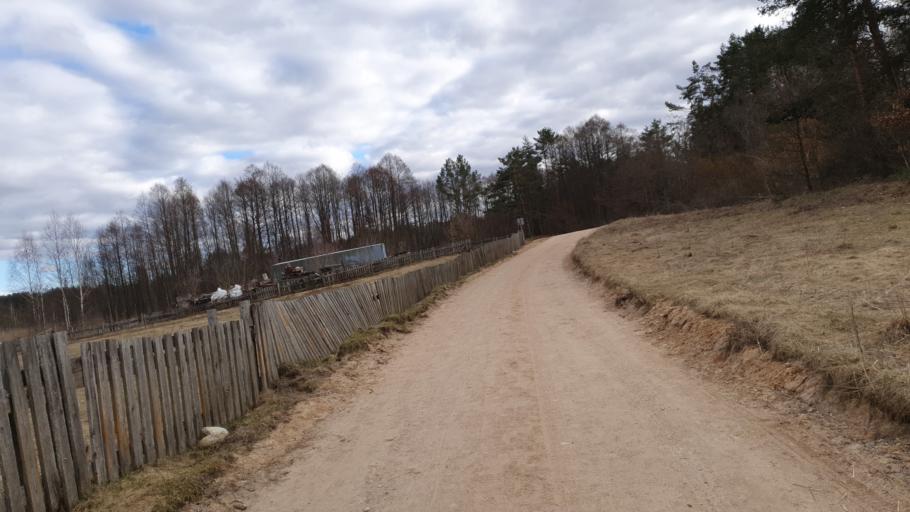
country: LT
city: Grigiskes
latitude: 54.7337
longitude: 25.0275
